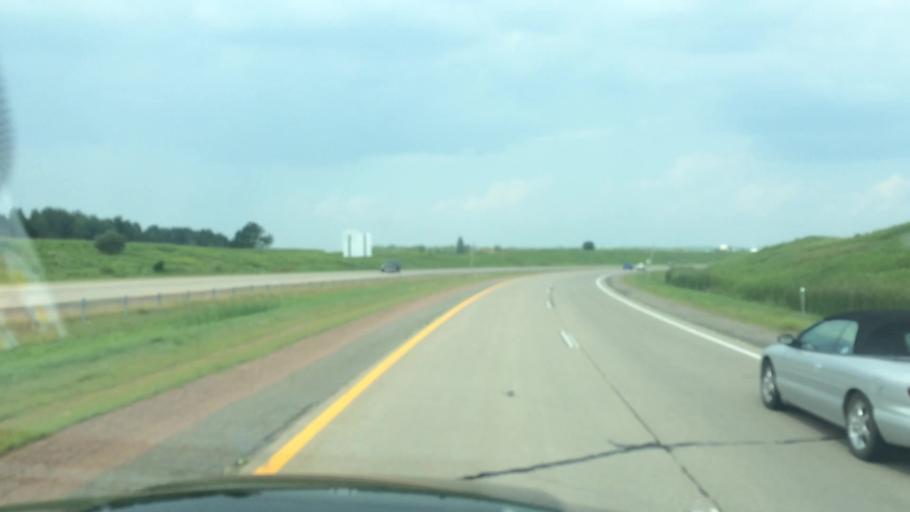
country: US
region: Wisconsin
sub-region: Clark County
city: Abbotsford
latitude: 44.9394
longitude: -90.2933
